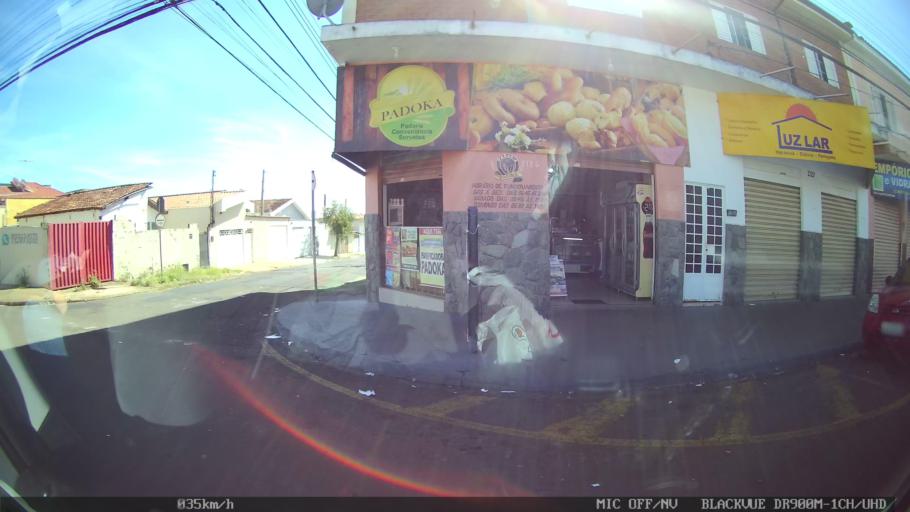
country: BR
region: Sao Paulo
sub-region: Franca
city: Franca
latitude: -20.5598
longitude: -47.4001
